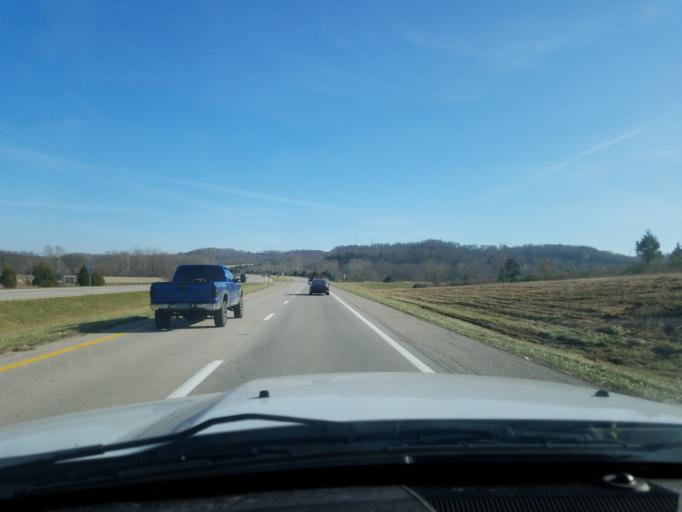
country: US
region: Ohio
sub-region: Adams County
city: Peebles
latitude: 38.9343
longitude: -83.4754
